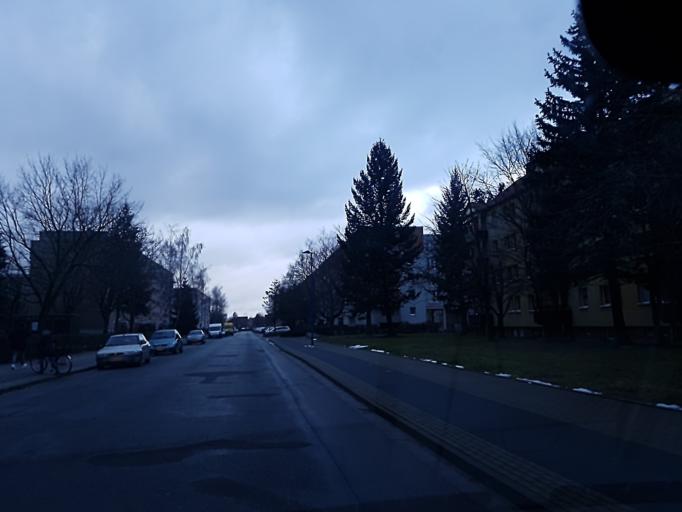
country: DE
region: Brandenburg
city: Finsterwalde
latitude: 51.6204
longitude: 13.7094
